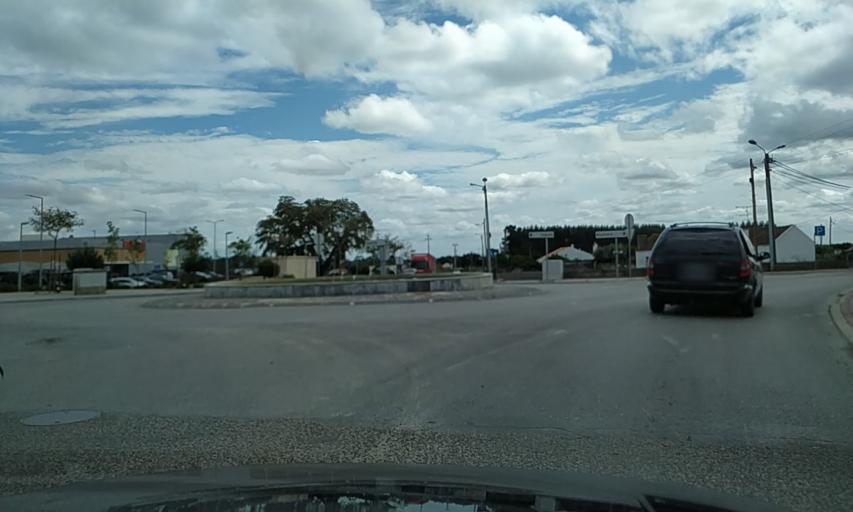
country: PT
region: Evora
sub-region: Vendas Novas
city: Vendas Novas
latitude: 38.6734
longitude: -8.4685
